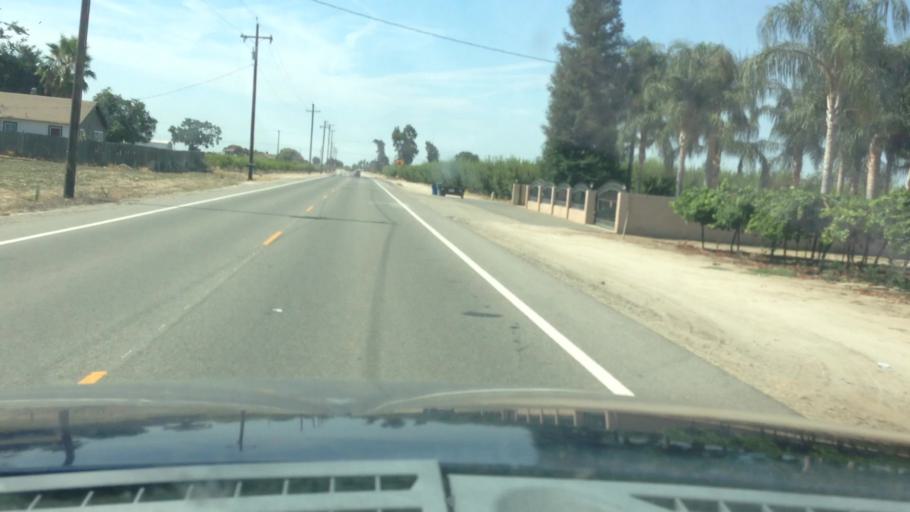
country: US
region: California
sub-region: Fresno County
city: Parlier
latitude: 36.5715
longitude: -119.5570
